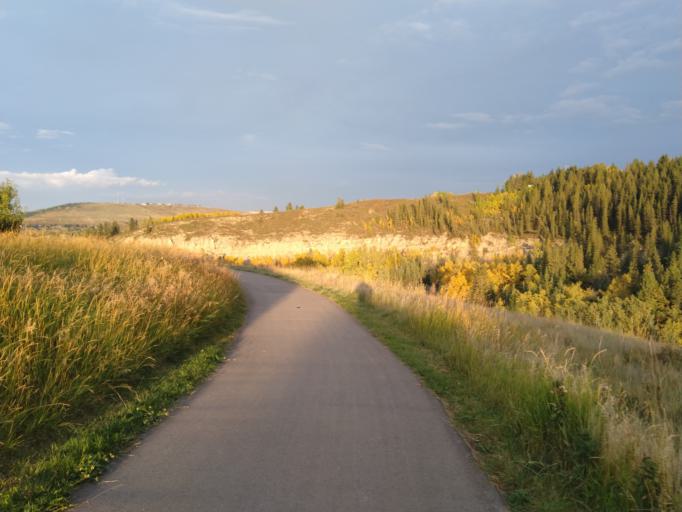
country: CA
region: Alberta
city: Cochrane
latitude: 51.1809
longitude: -114.5028
